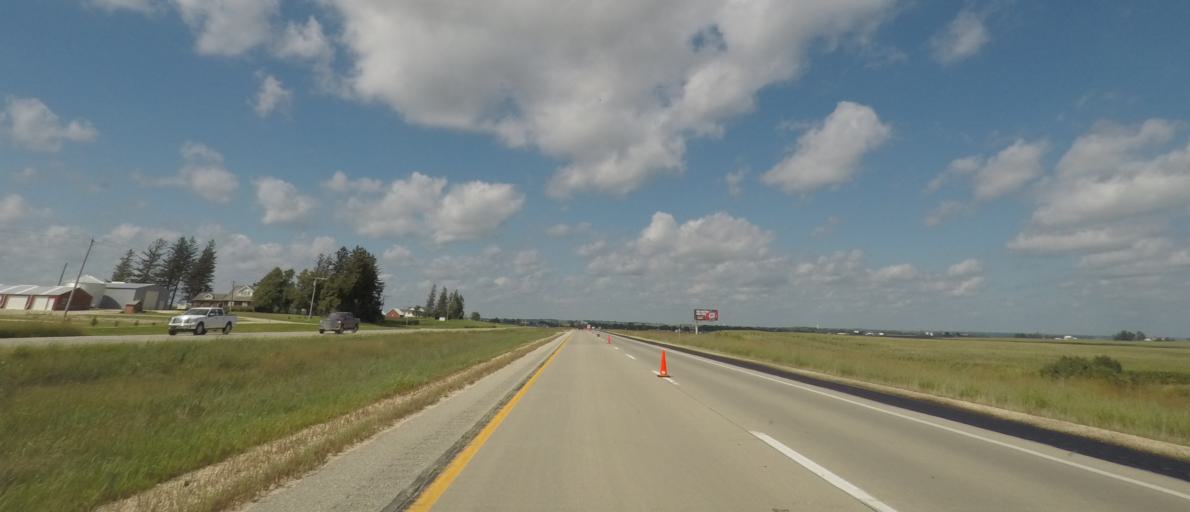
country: US
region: Iowa
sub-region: Jones County
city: Monticello
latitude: 42.1705
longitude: -91.2287
